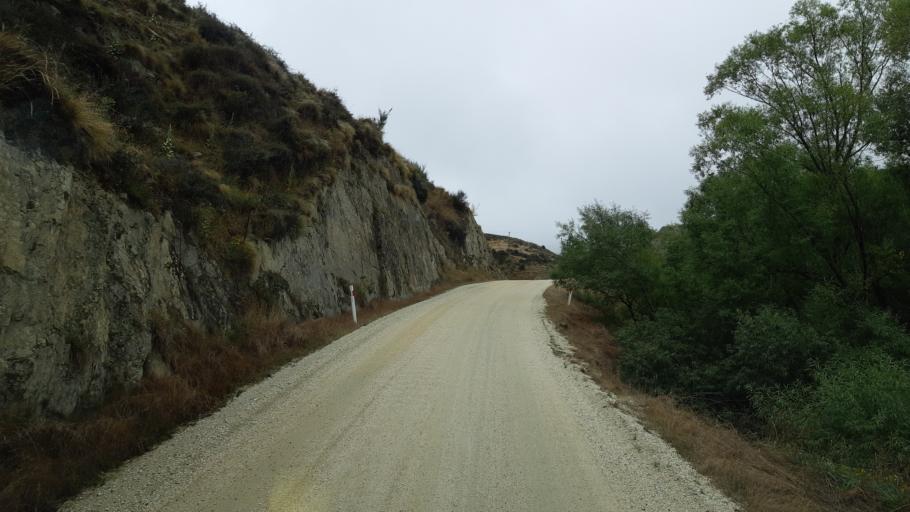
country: NZ
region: Otago
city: Oamaru
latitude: -44.9736
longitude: 170.5160
